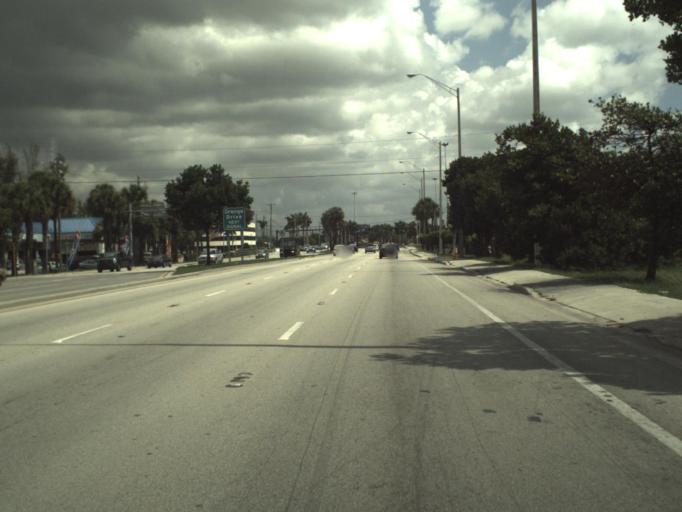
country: US
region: Florida
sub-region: Broward County
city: Davie
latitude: 26.0638
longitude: -80.2078
